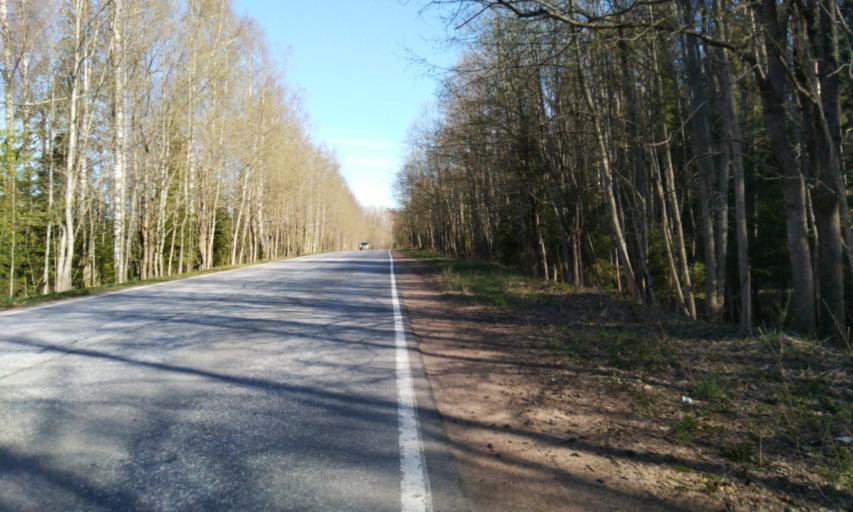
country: RU
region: Leningrad
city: Garbolovo
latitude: 60.3655
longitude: 30.4419
